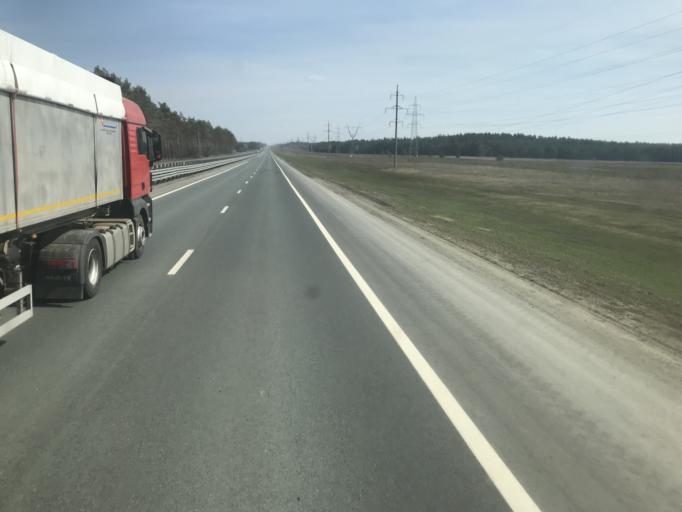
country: RU
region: Samara
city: Povolzhskiy
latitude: 53.5149
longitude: 49.6600
